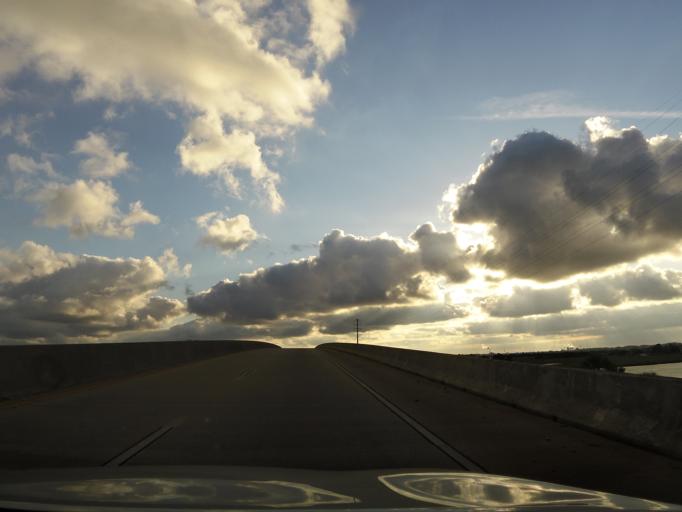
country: US
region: Georgia
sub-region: Glynn County
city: Saint Simon Mills
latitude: 31.1652
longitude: -81.4446
